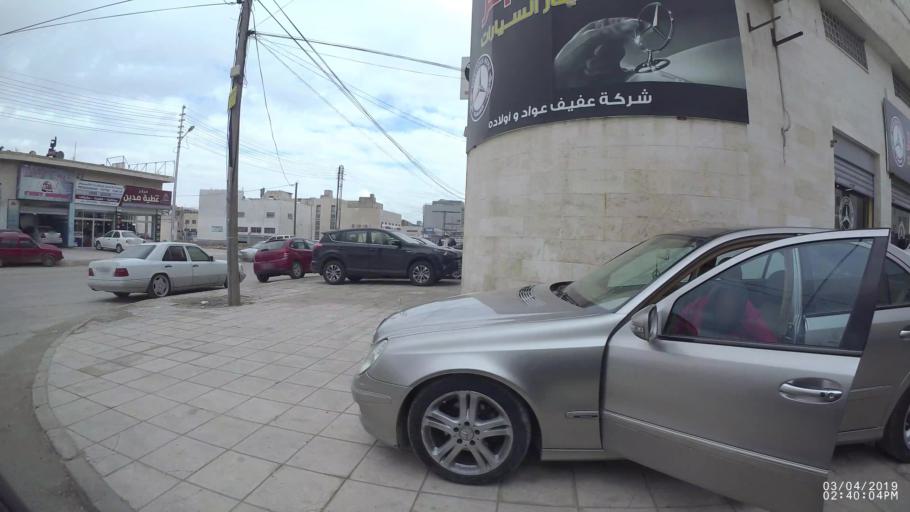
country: JO
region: Amman
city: Wadi as Sir
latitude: 31.9429
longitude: 35.8391
